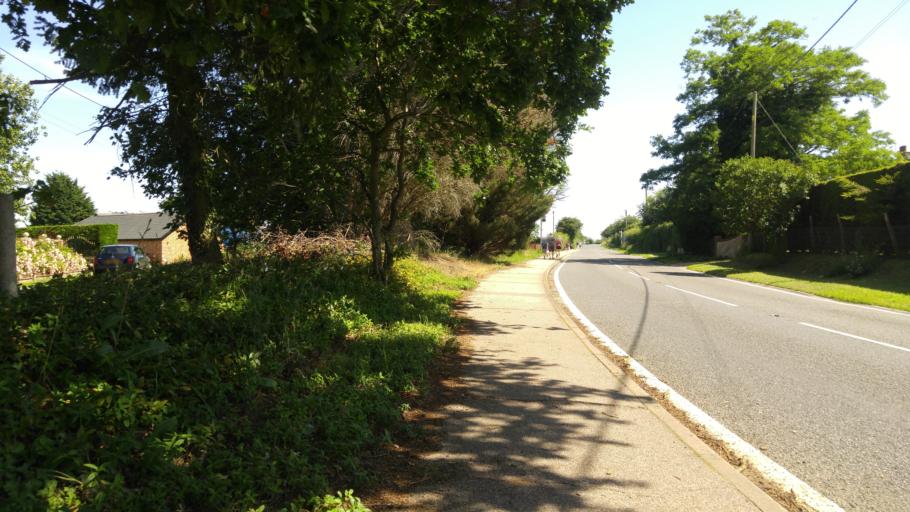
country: GB
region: England
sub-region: Essex
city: Rowhedge
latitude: 51.8636
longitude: 0.9359
